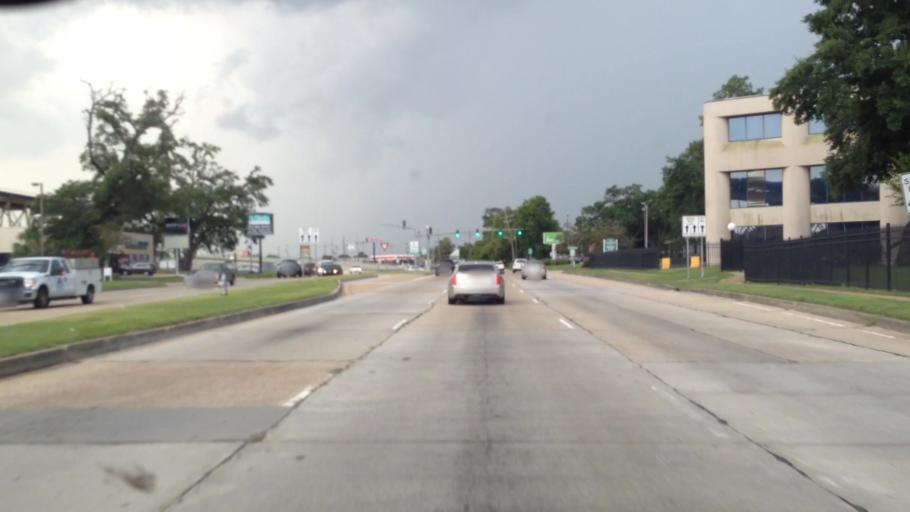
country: US
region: Louisiana
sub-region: Jefferson Parish
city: Elmwood
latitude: 29.9573
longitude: -90.1829
